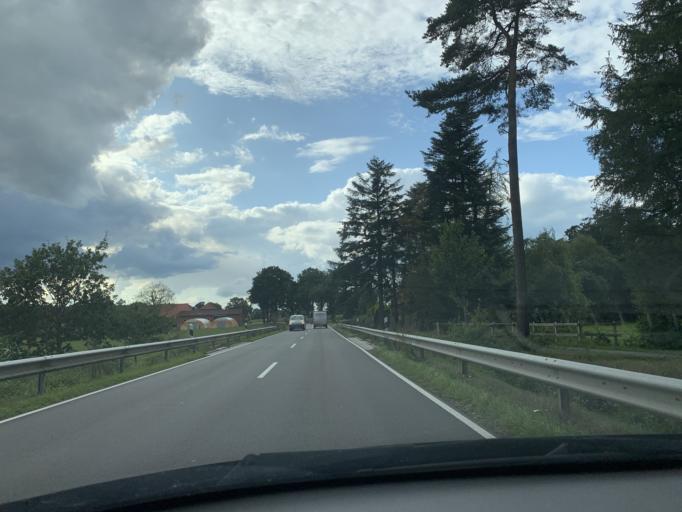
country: DE
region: Lower Saxony
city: Westerstede
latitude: 53.2868
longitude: 8.0179
